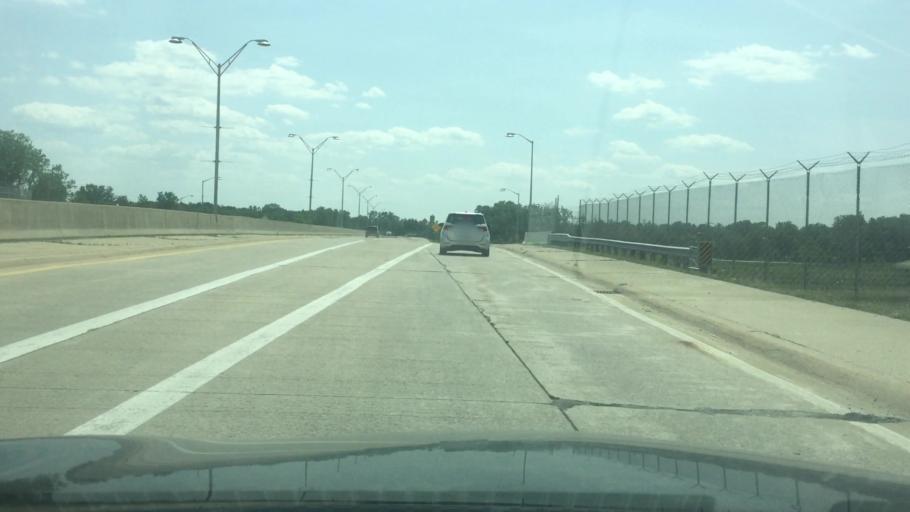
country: US
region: Michigan
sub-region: Wayne County
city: Romulus
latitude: 42.1954
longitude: -83.3634
